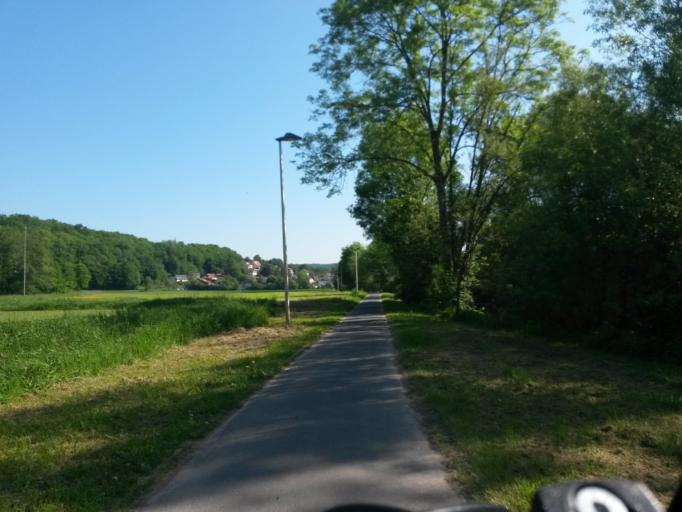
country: DE
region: Bavaria
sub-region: Regierungsbezirk Unterfranken
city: Bad Kissingen
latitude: 50.2317
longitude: 10.0663
